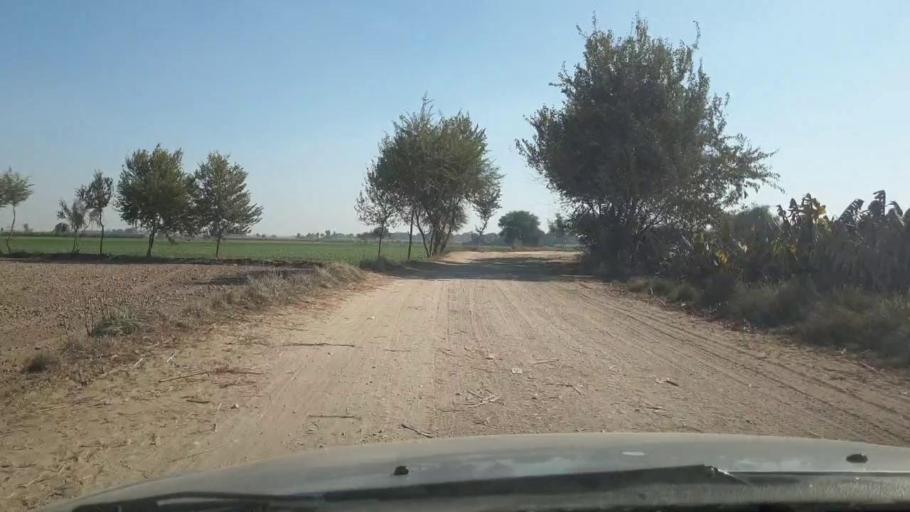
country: PK
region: Sindh
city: Ghotki
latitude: 28.0222
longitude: 69.2219
